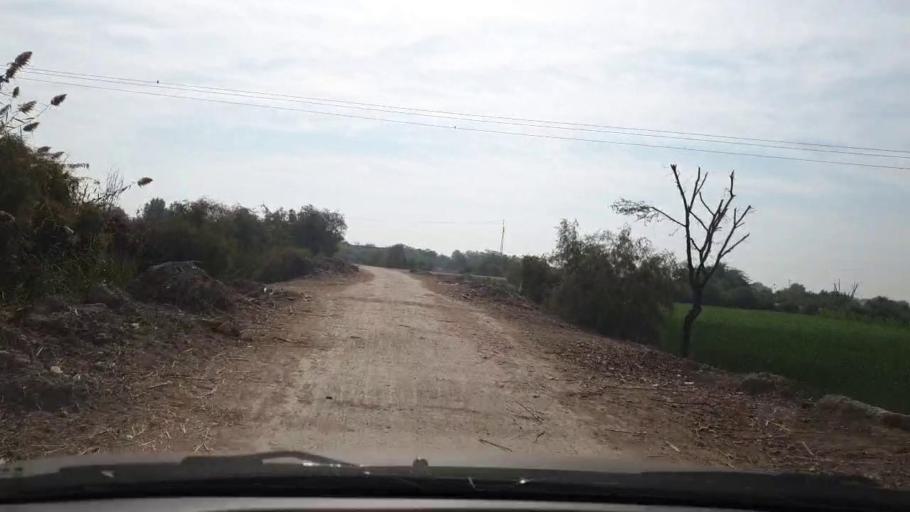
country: PK
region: Sindh
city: Shahpur Chakar
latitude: 26.1738
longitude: 68.6792
